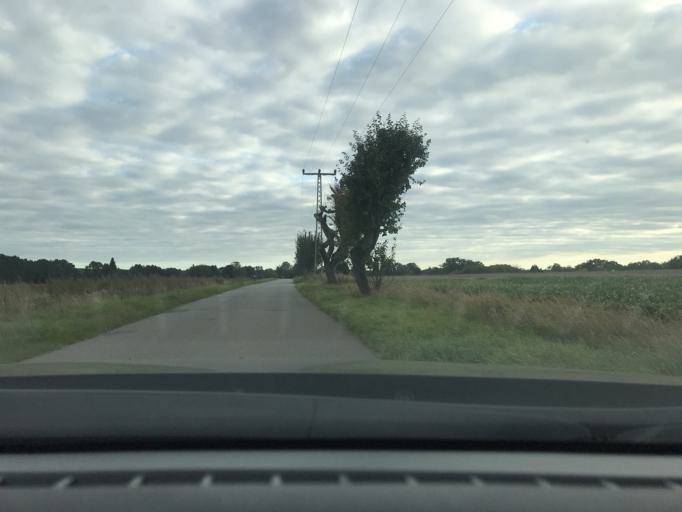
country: DE
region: Lower Saxony
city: Suderburg
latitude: 52.9035
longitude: 10.4539
